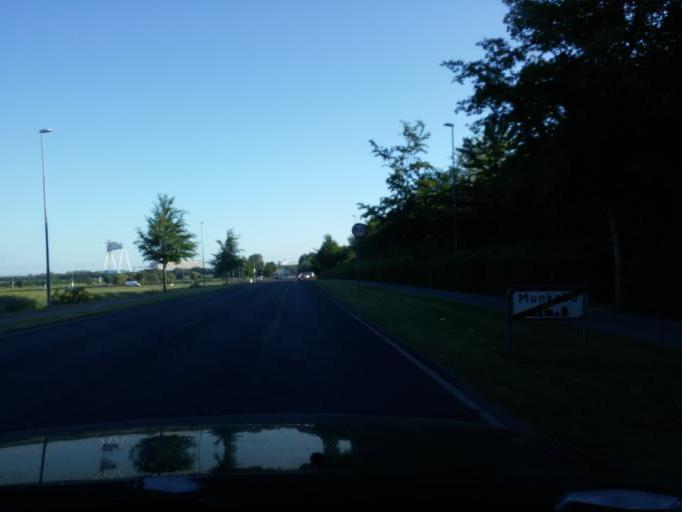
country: DK
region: South Denmark
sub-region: Kerteminde Kommune
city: Munkebo
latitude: 55.4494
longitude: 10.5419
